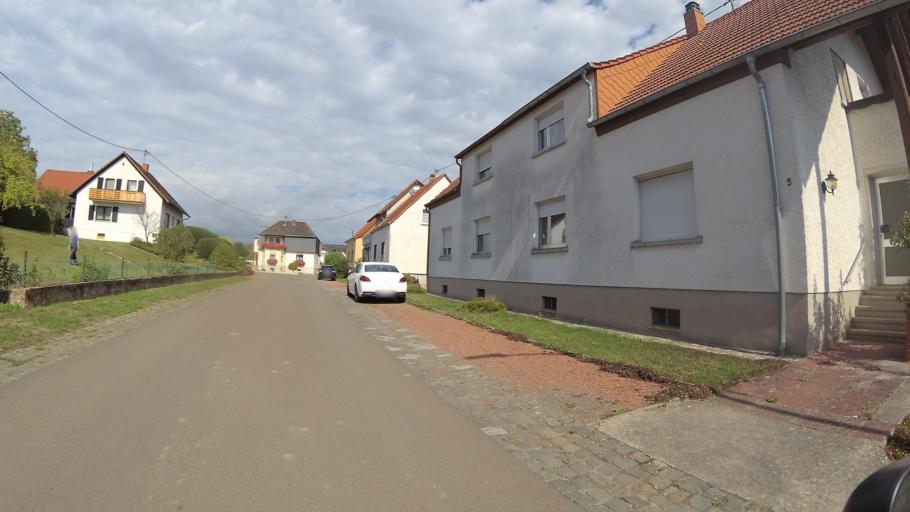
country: DE
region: Saarland
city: Gersheim
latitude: 49.1332
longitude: 7.2031
